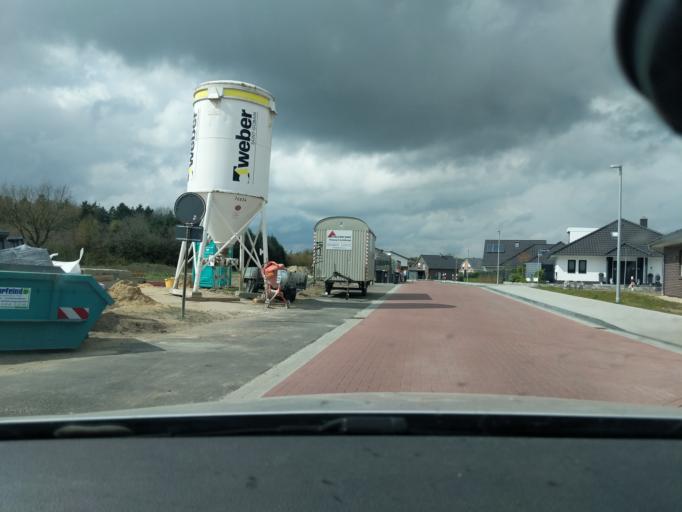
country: DE
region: Lower Saxony
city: Stade
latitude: 53.5671
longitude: 9.4687
